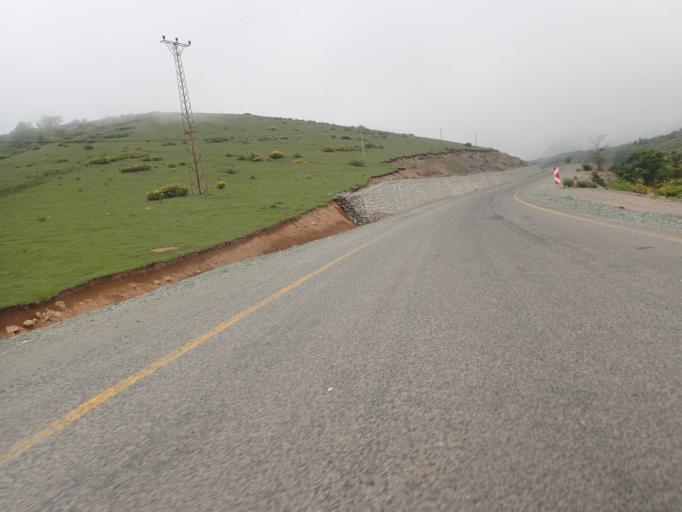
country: TR
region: Ordu
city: Topcam
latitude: 40.6751
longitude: 37.9304
